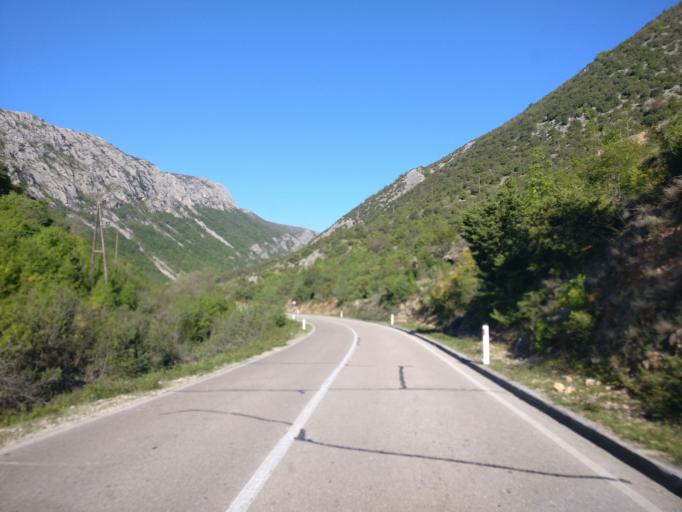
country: BA
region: Federation of Bosnia and Herzegovina
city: Stolac
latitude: 43.0721
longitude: 18.0448
